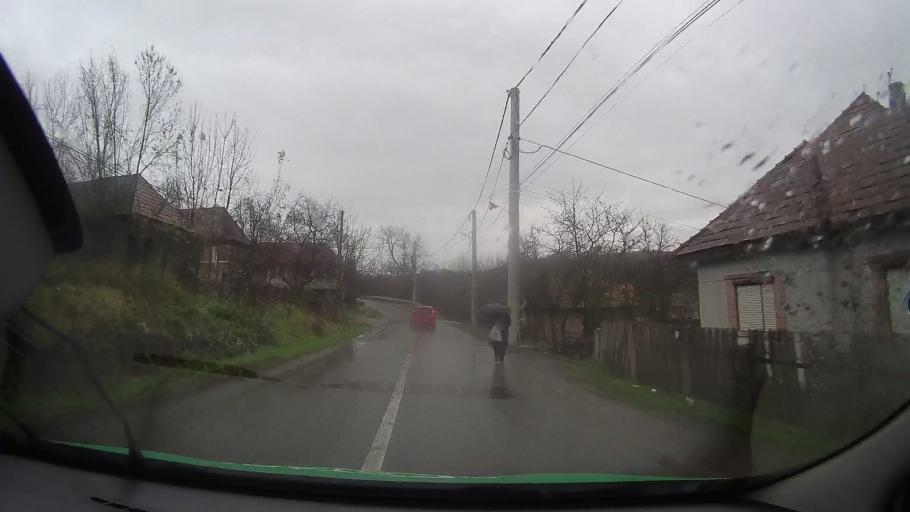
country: RO
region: Mures
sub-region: Comuna Vatava
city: Vatava
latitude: 46.9383
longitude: 24.7675
